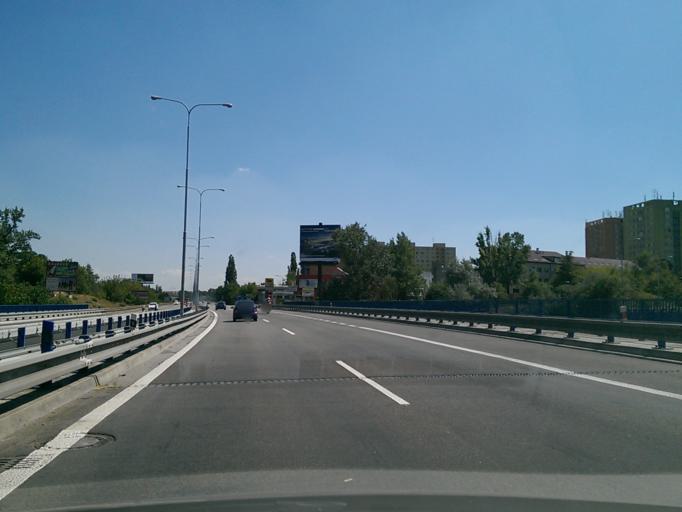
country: CZ
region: South Moravian
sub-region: Mesto Brno
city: Mokra Hora
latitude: 49.2361
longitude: 16.5903
